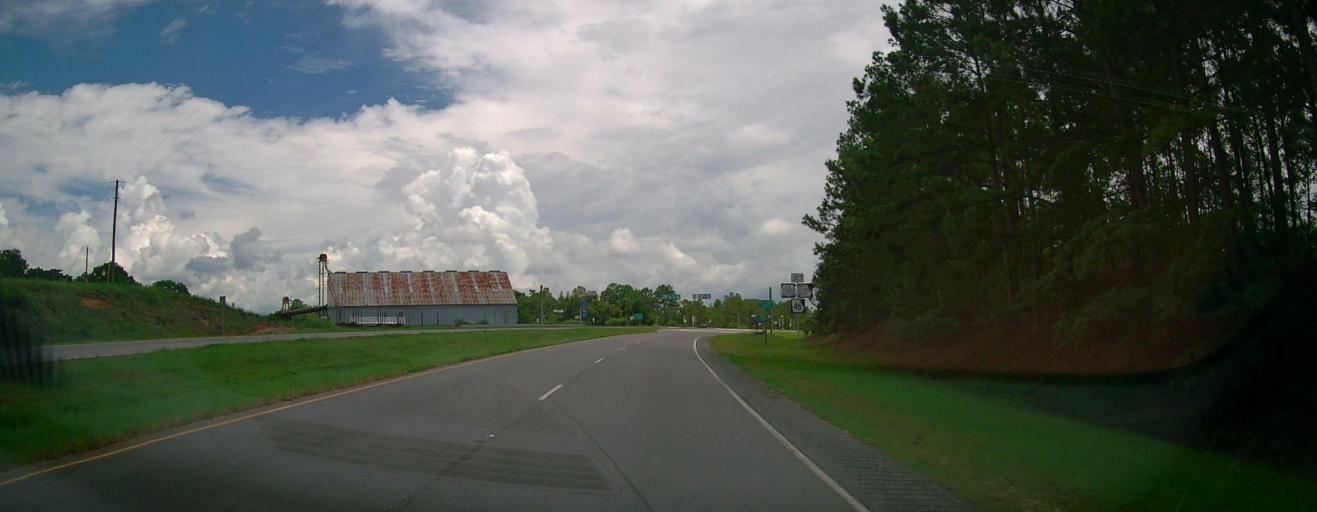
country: US
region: Georgia
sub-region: Dodge County
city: Eastman
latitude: 32.1966
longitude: -83.2115
